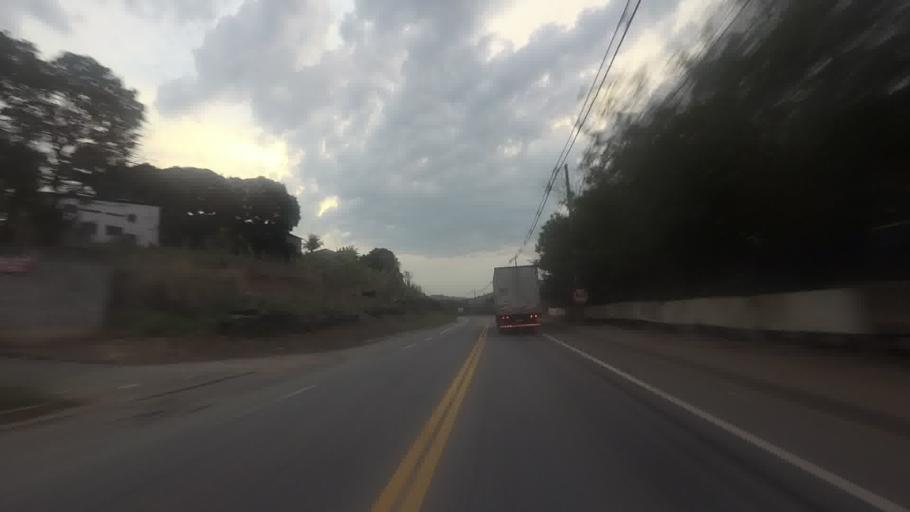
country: BR
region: Minas Gerais
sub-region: Alem Paraiba
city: Alem Paraiba
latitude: -21.8775
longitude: -42.6723
